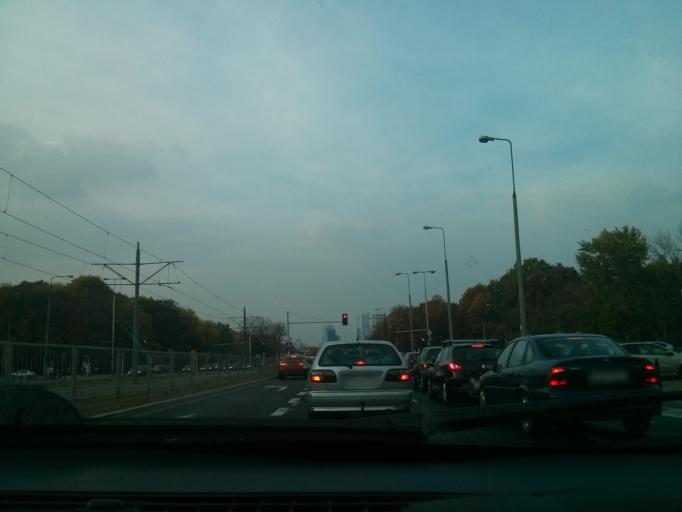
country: PL
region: Masovian Voivodeship
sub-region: Warszawa
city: Warsaw
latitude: 52.2097
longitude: 21.0076
